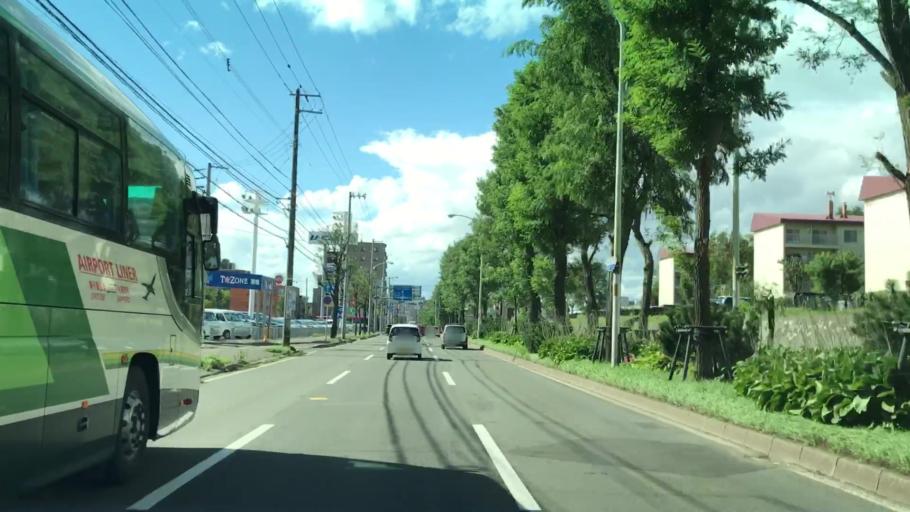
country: JP
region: Hokkaido
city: Sapporo
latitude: 43.0315
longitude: 141.4317
